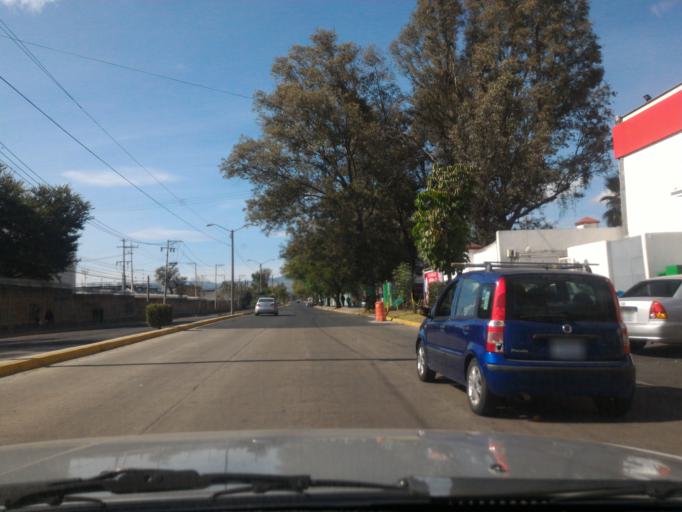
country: MX
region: Jalisco
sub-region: Tlajomulco de Zuniga
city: La Tijera
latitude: 20.6119
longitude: -103.4161
